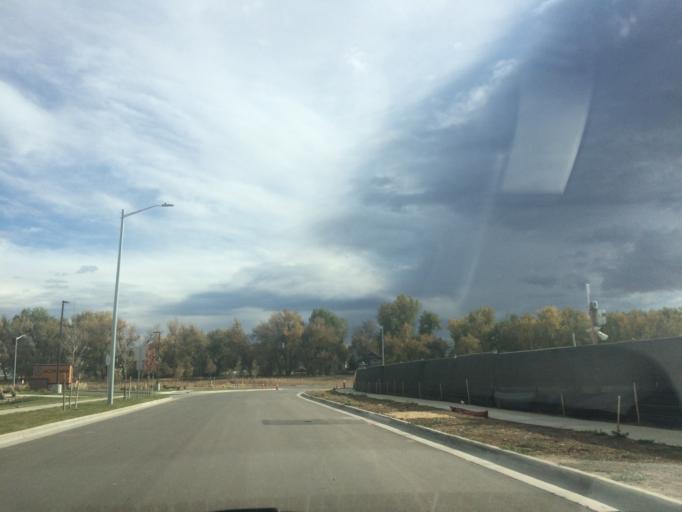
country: US
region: Colorado
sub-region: Boulder County
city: Longmont
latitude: 40.1364
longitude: -105.1279
